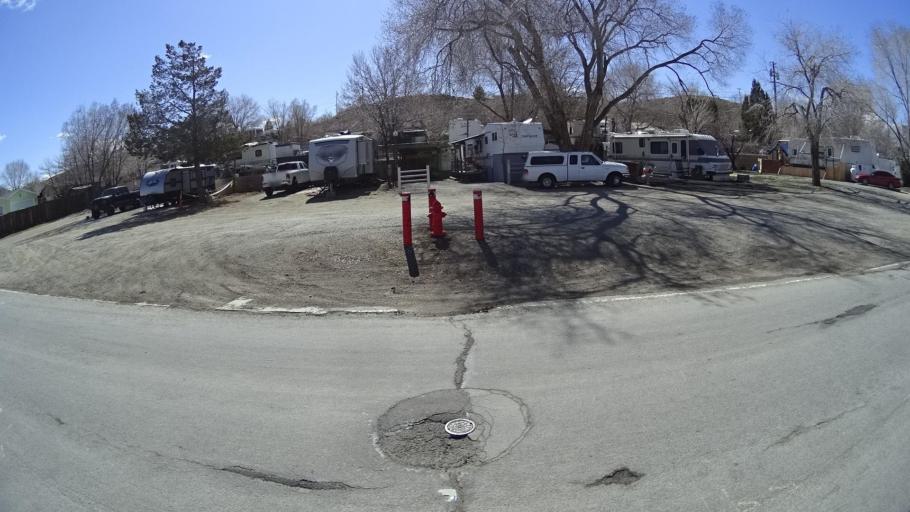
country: US
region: Nevada
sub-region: Washoe County
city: Golden Valley
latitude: 39.5881
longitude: -119.8190
